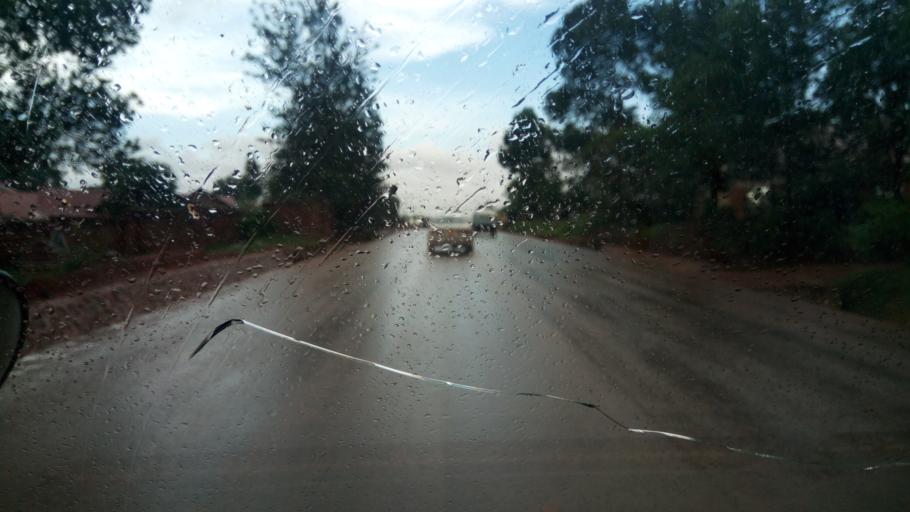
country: UG
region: Central Region
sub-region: Wakiso District
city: Wakiso
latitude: 0.3915
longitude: 32.5051
